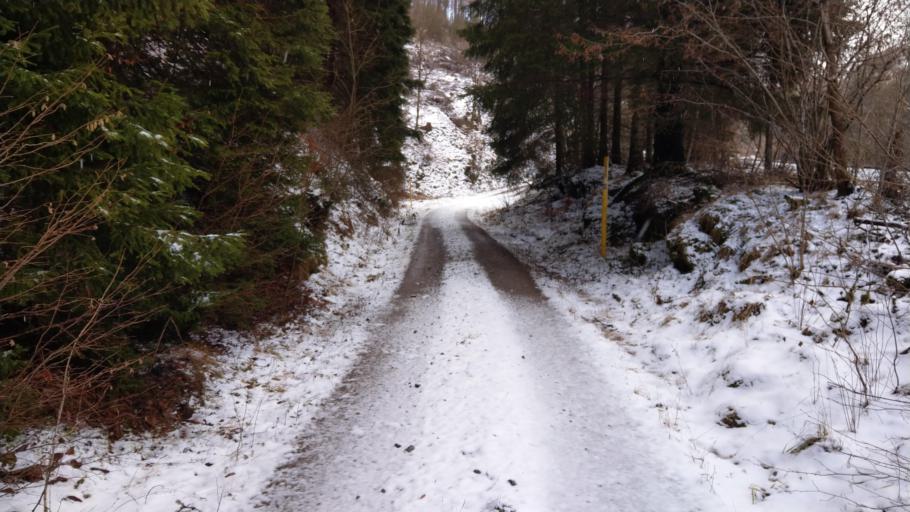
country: DE
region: Hesse
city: Willingen
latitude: 51.3134
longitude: 8.5853
